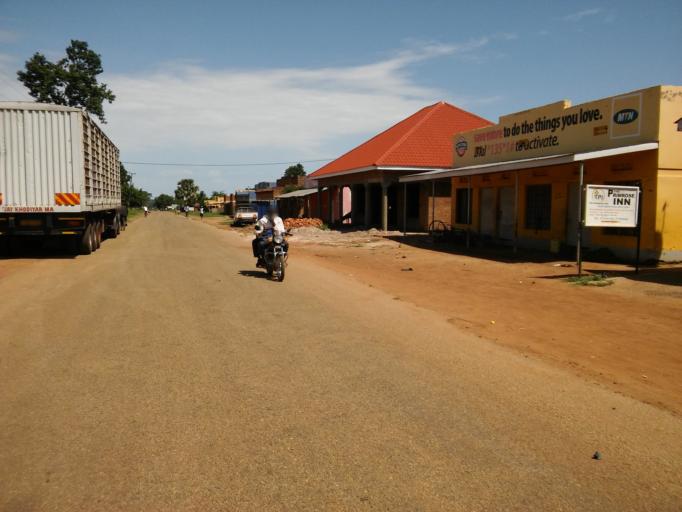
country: UG
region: Eastern Region
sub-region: Kumi District
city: Kumi
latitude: 1.4868
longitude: 33.9285
